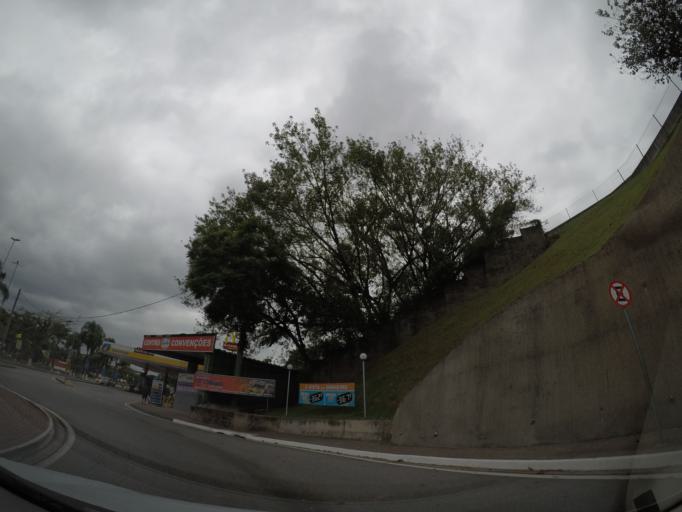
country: BR
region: Sao Paulo
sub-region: Louveira
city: Louveira
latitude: -23.0898
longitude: -46.9741
